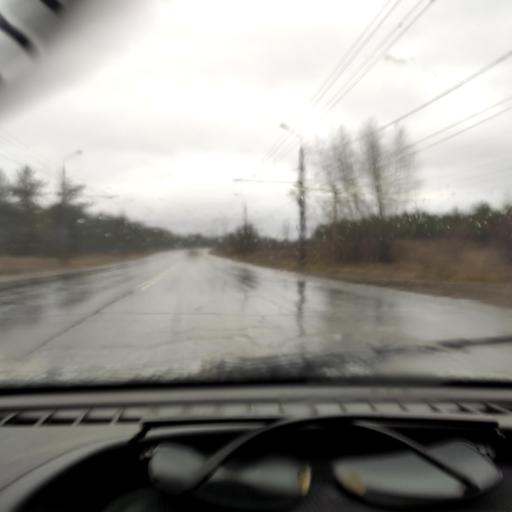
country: RU
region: Samara
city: Zhigulevsk
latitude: 53.5031
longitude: 49.5152
